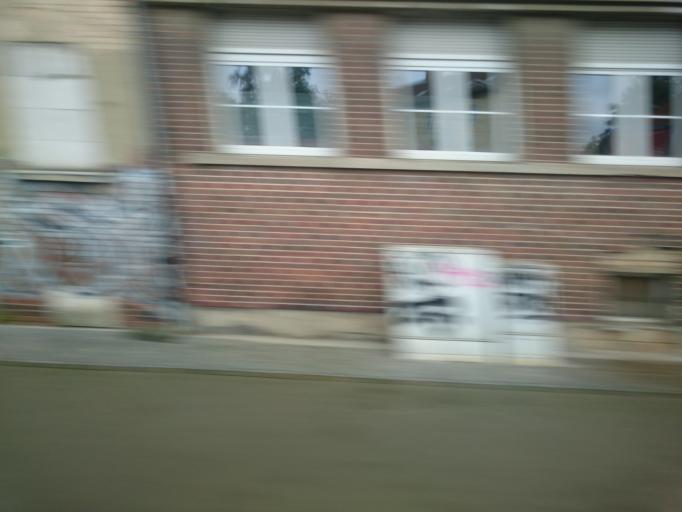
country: DE
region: Saxony-Anhalt
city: Halle (Saale)
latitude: 51.4944
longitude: 12.0066
